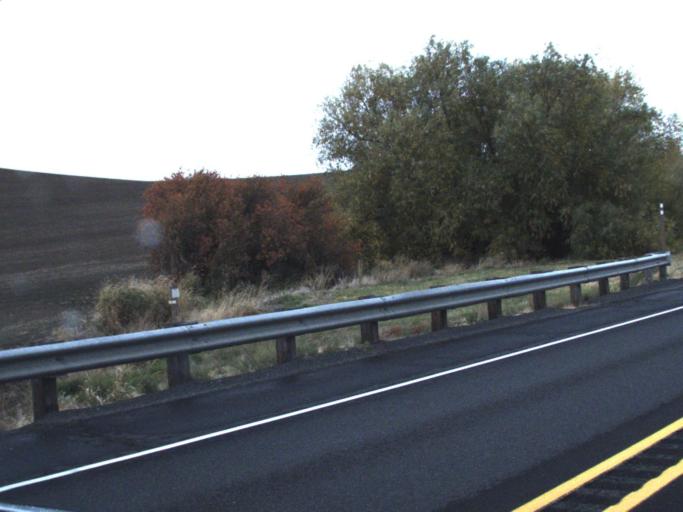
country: US
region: Washington
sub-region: Whitman County
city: Pullman
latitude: 46.7406
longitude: -117.2306
